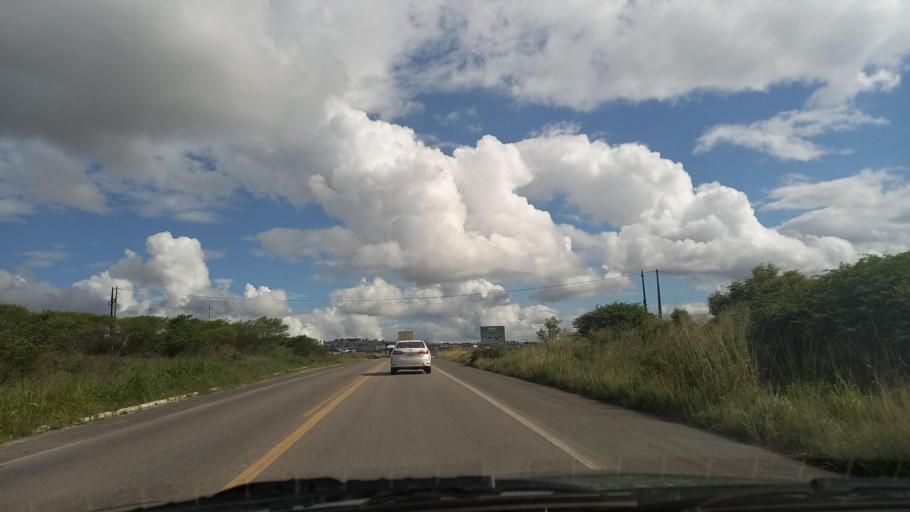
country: BR
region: Pernambuco
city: Garanhuns
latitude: -8.8402
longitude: -36.4576
